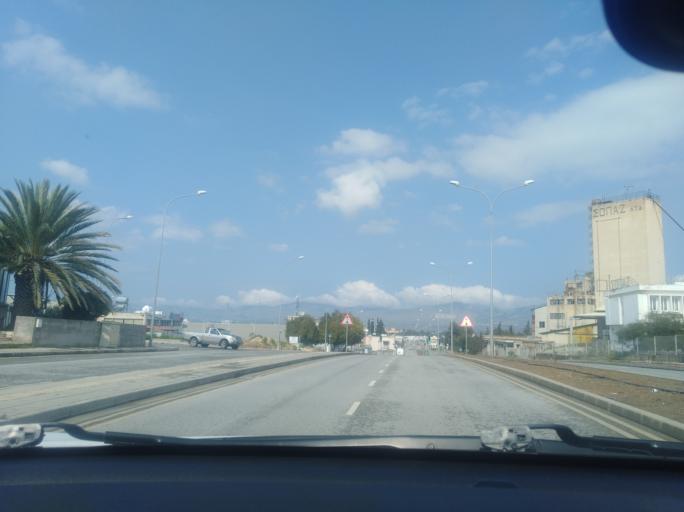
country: CY
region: Lefkosia
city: Nicosia
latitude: 35.1749
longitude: 33.3963
